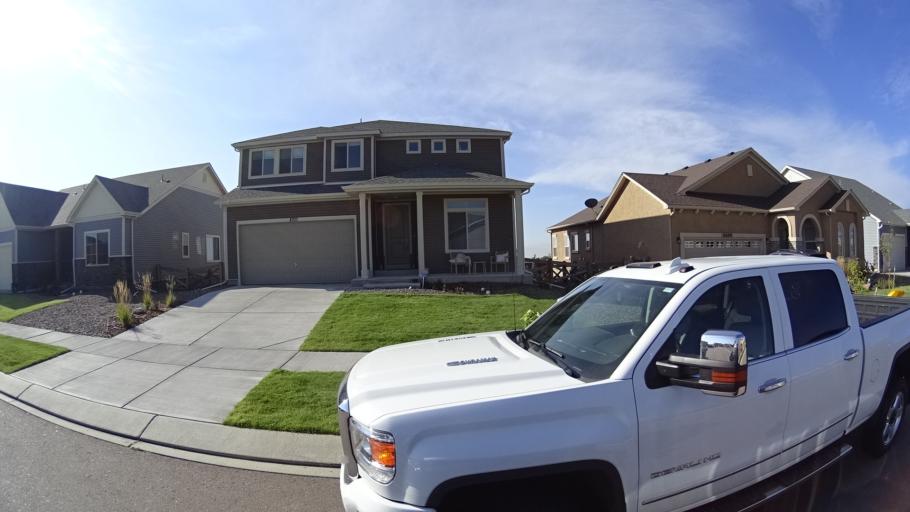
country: US
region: Colorado
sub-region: El Paso County
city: Cimarron Hills
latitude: 38.9274
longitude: -104.6656
